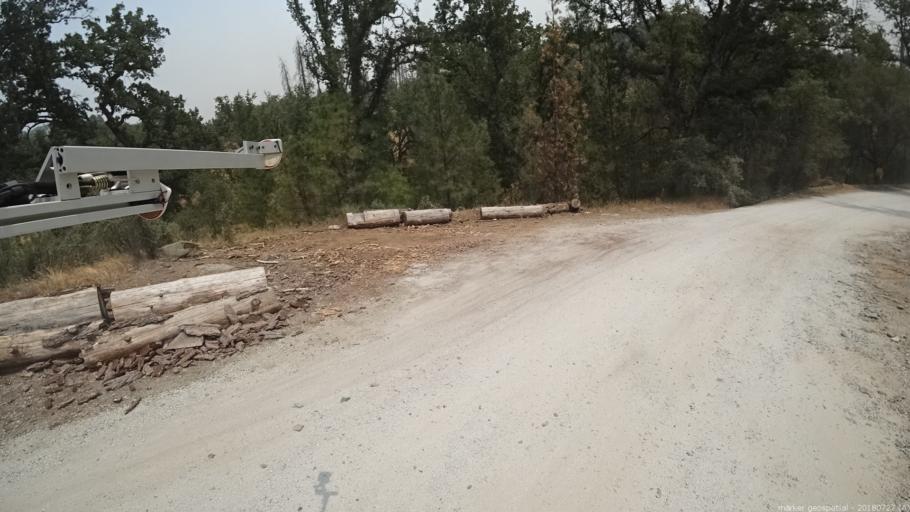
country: US
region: California
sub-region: Madera County
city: Coarsegold
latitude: 37.2840
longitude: -119.6720
